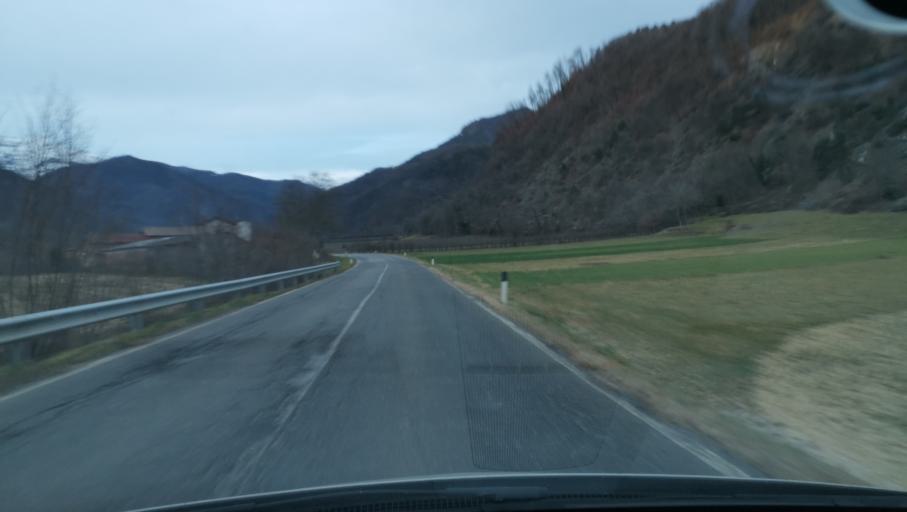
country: IT
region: Piedmont
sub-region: Provincia di Cuneo
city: Valgrana
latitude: 44.4128
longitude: 7.3536
